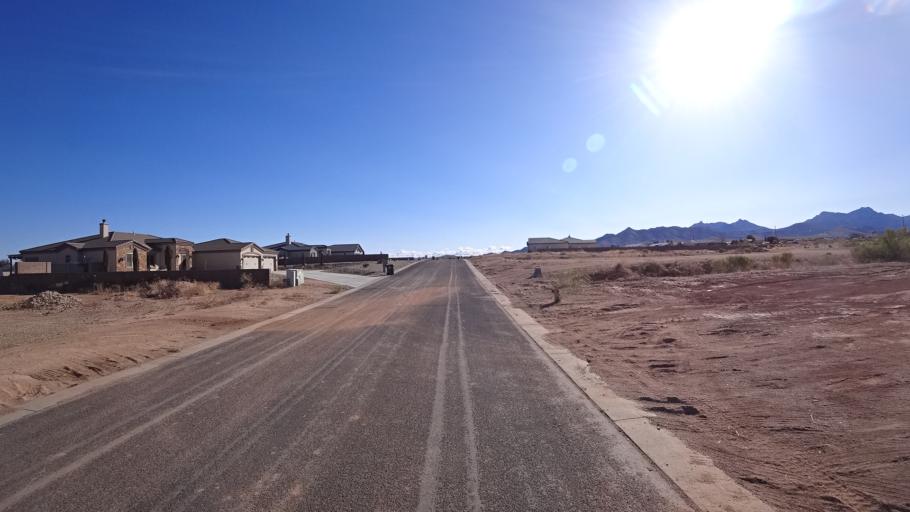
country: US
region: Arizona
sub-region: Mohave County
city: Kingman
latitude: 35.2004
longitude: -114.0009
